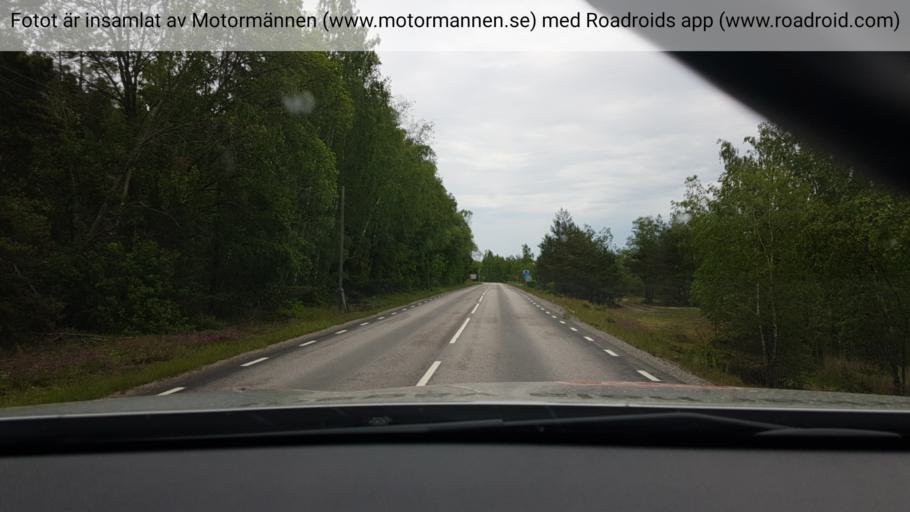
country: SE
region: Stockholm
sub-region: Nynashamns Kommun
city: Nynashamn
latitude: 58.9591
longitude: 18.0213
